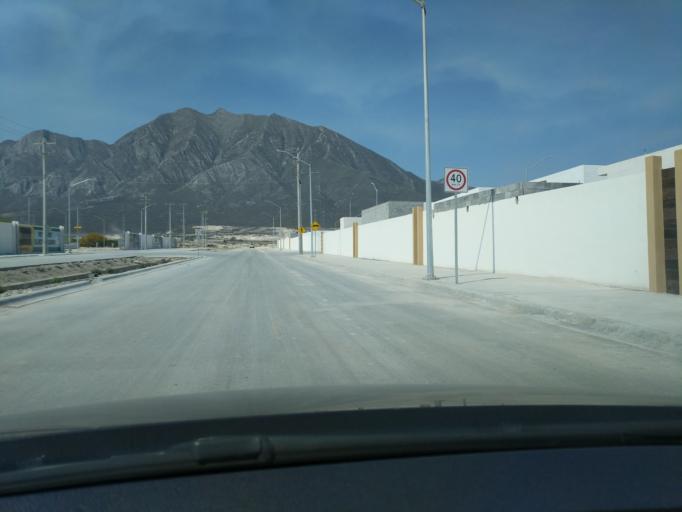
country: MX
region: Nuevo Leon
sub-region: Garcia
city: Valle de Lincoln
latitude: 25.7962
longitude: -100.4713
